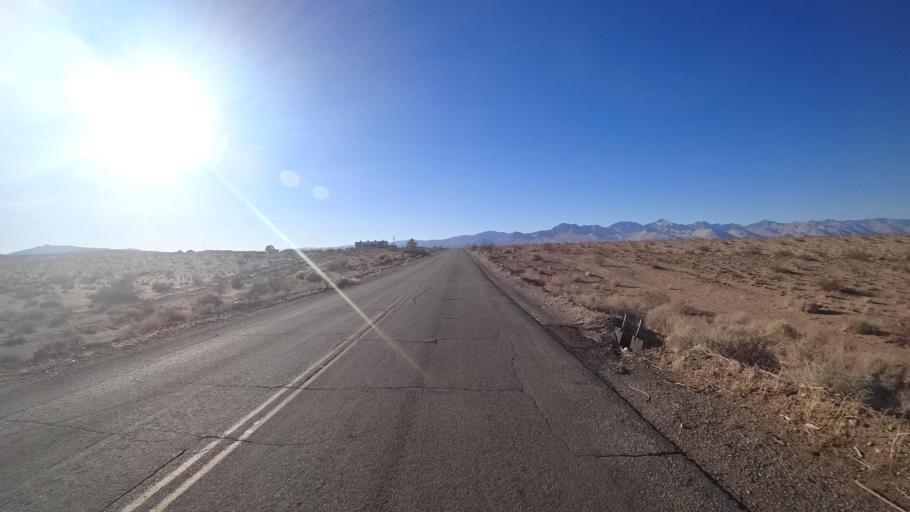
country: US
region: California
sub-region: Kern County
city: China Lake Acres
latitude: 35.6083
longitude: -117.7330
